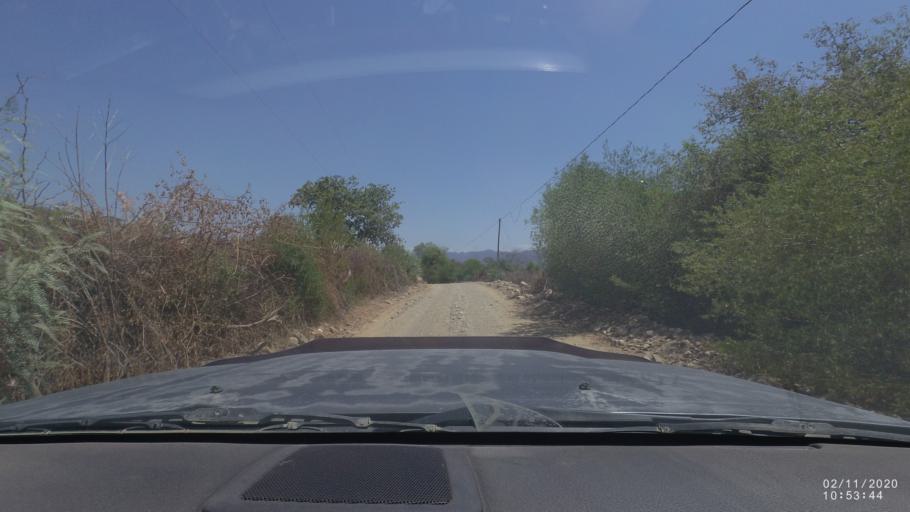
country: BO
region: Cochabamba
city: Aiquile
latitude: -18.1768
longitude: -64.8695
